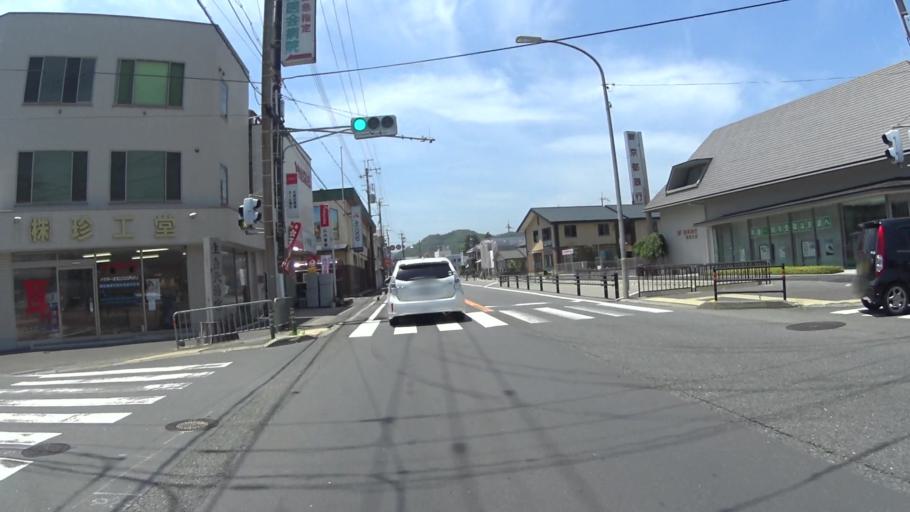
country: JP
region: Kyoto
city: Kameoka
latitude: 35.1095
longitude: 135.4739
